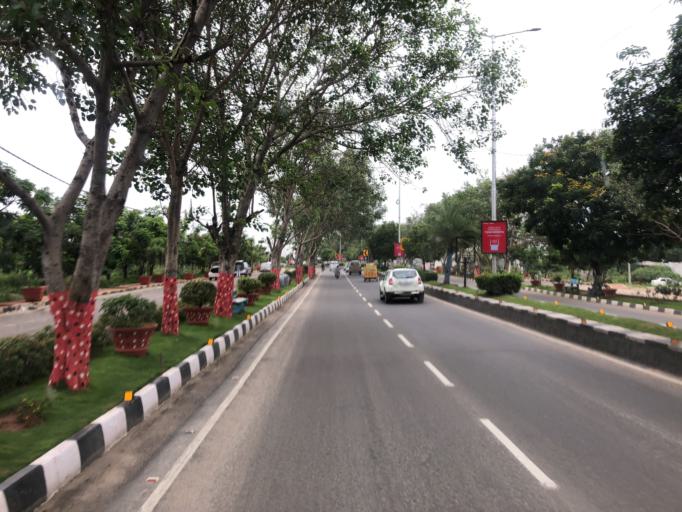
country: IN
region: Telangana
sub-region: Rangareddi
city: Kukatpalli
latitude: 17.4616
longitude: 78.3766
